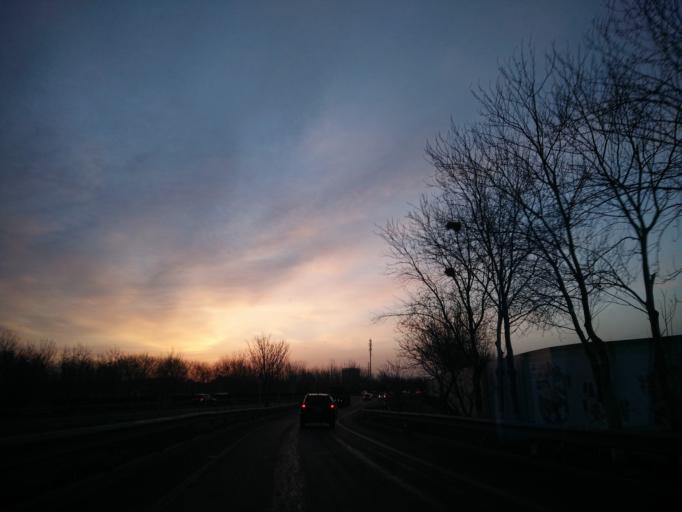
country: CN
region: Beijing
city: Jiugong
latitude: 39.8166
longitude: 116.5011
